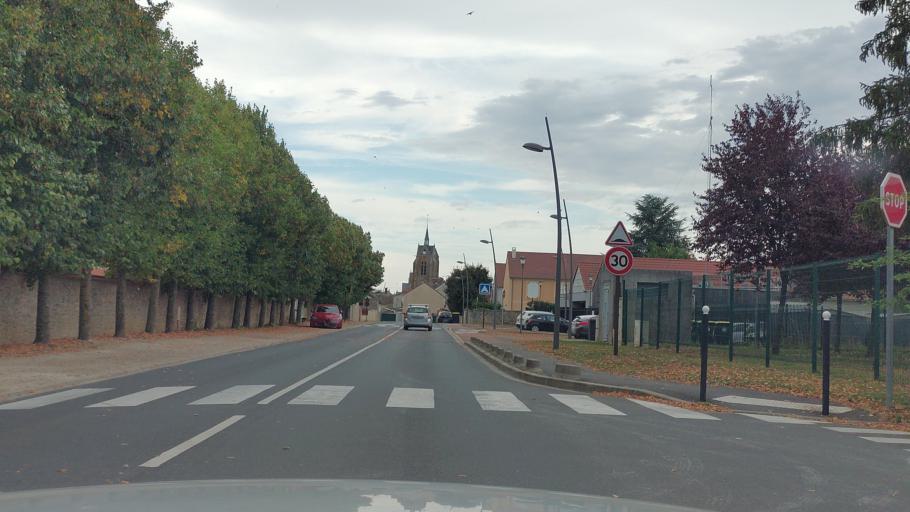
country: FR
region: Ile-de-France
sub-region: Departement de Seine-et-Marne
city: Mormant
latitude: 48.6034
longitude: 2.8903
